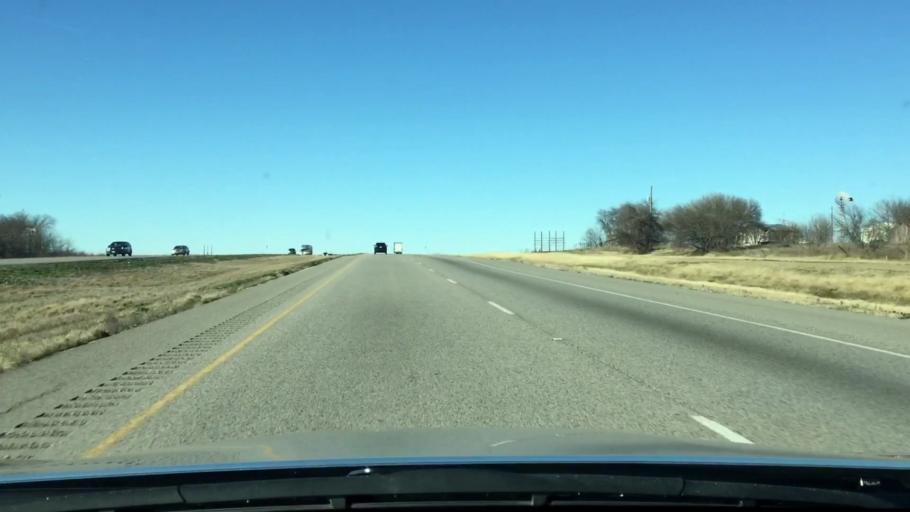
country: US
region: Texas
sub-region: Hill County
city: Itasca
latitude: 32.1184
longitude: -97.1155
